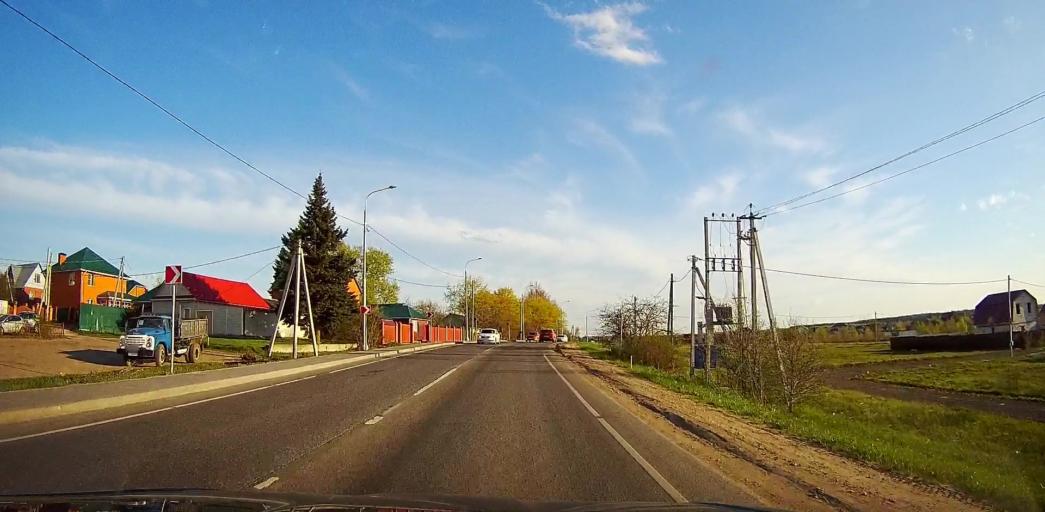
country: RU
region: Moskovskaya
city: Bronnitsy
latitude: 55.3383
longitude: 38.2220
